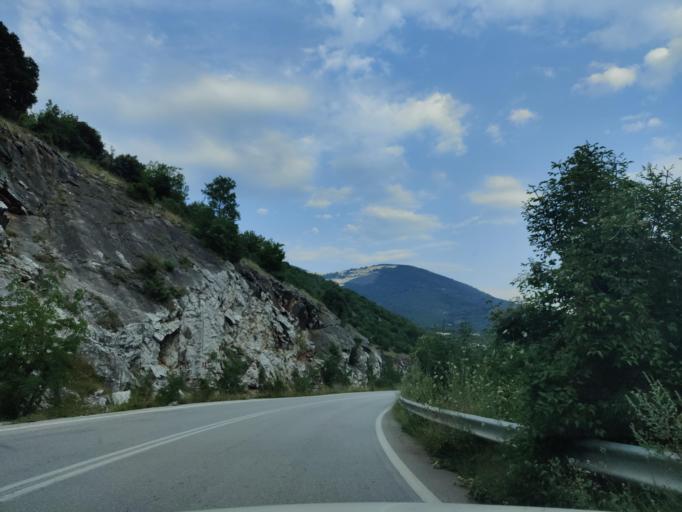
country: GR
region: East Macedonia and Thrace
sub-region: Nomos Dramas
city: Volakas
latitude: 41.2838
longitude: 23.9721
